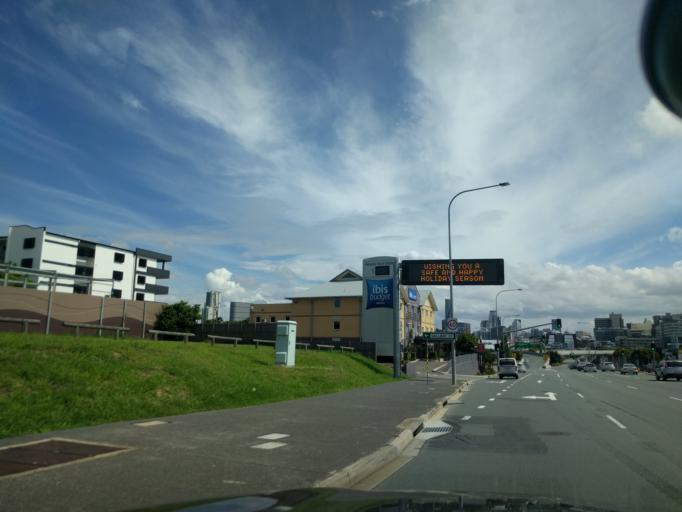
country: AU
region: Queensland
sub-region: Brisbane
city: Windsor
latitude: -27.4390
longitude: 153.0311
